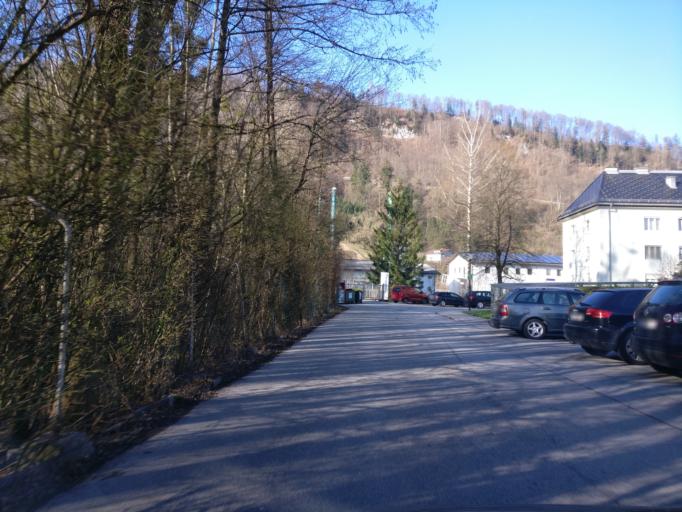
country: AT
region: Salzburg
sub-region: Politischer Bezirk Hallein
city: Hallein
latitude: 47.6755
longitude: 13.1037
